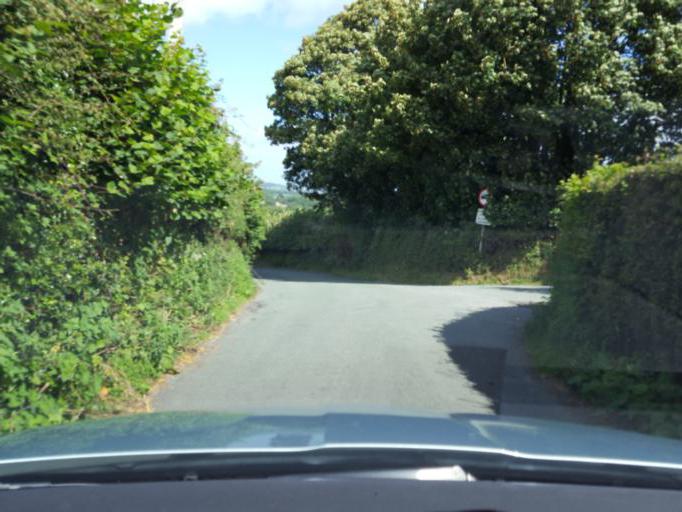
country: GB
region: Wales
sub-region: County of Flintshire
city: Leeswood
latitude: 53.1198
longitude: -3.1333
